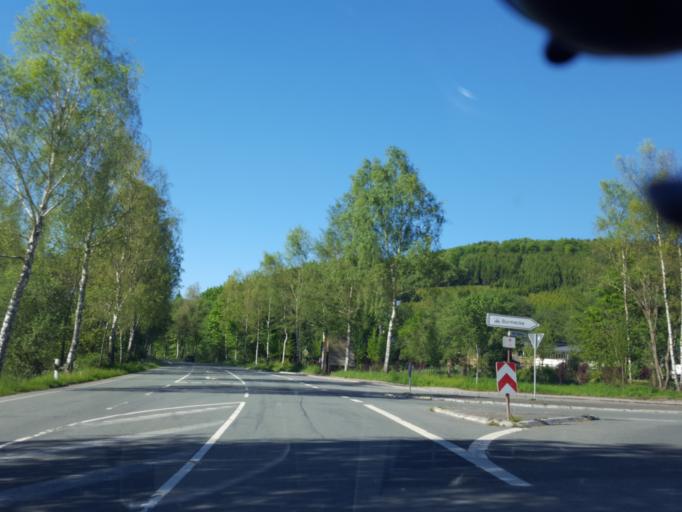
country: DE
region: North Rhine-Westphalia
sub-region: Regierungsbezirk Arnsberg
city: Winterberg
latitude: 51.2379
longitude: 8.4843
